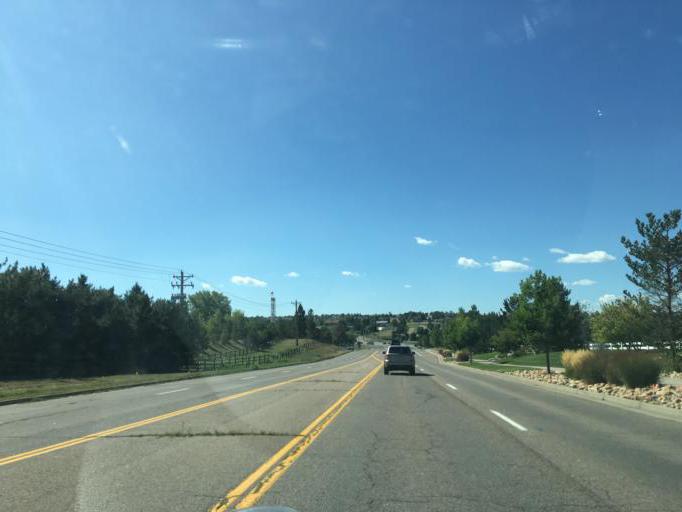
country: US
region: Colorado
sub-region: Douglas County
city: Parker
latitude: 39.5994
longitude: -104.7449
